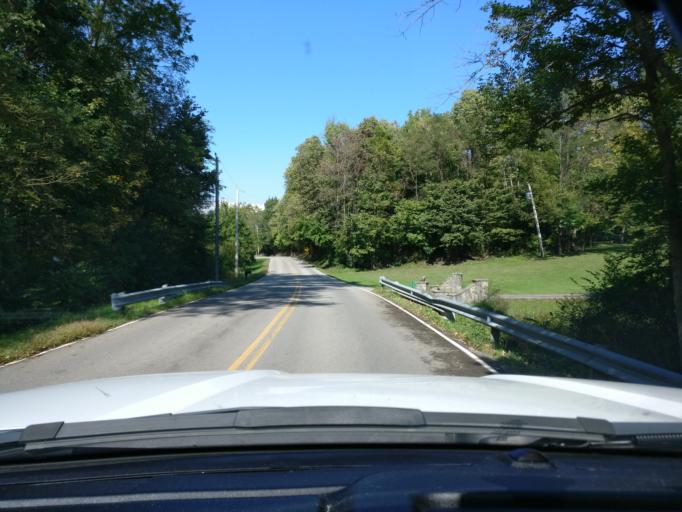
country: US
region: Ohio
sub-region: Warren County
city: Waynesville
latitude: 39.4888
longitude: -83.9972
